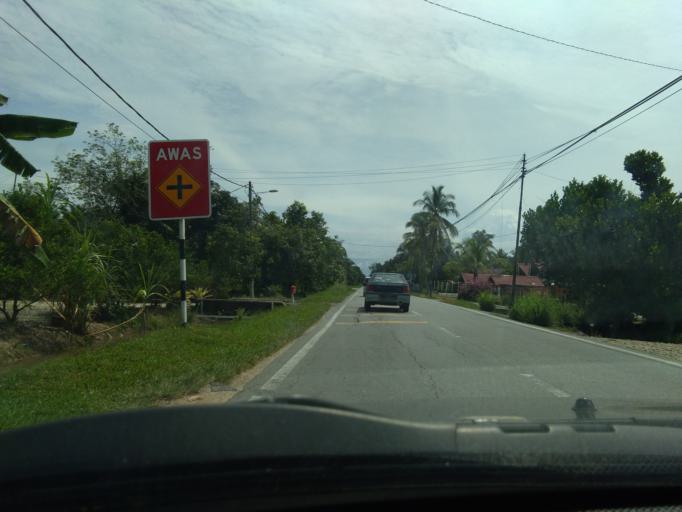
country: MY
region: Perak
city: Bagan Serai
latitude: 5.0440
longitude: 100.5781
